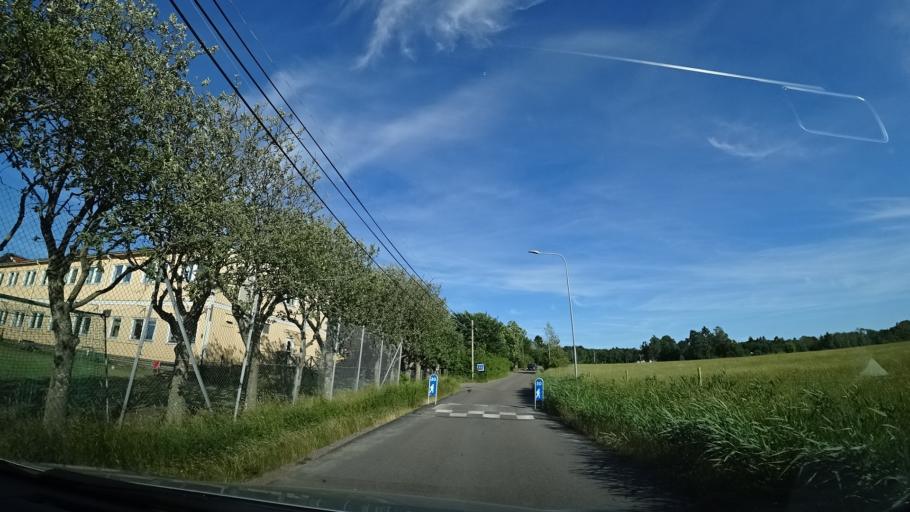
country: SE
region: Vaestra Goetaland
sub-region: Goteborg
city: Billdal
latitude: 57.5794
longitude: 11.9591
